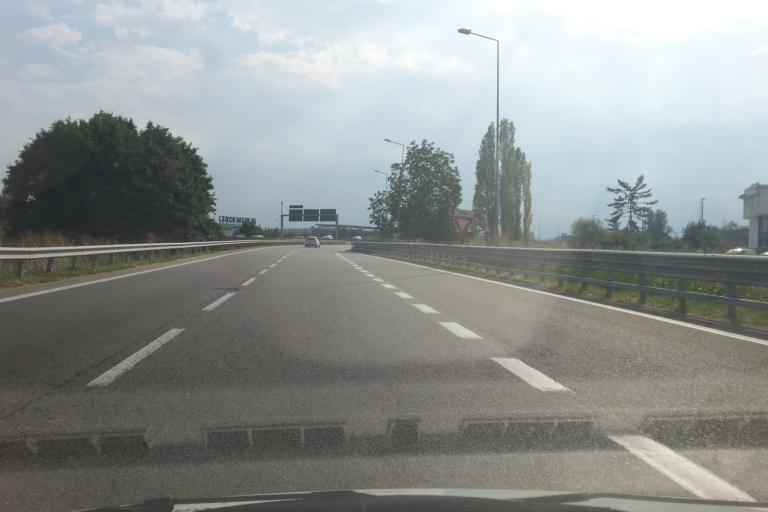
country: IT
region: Piedmont
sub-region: Provincia di Torino
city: Savonera
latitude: 45.1051
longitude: 7.5971
